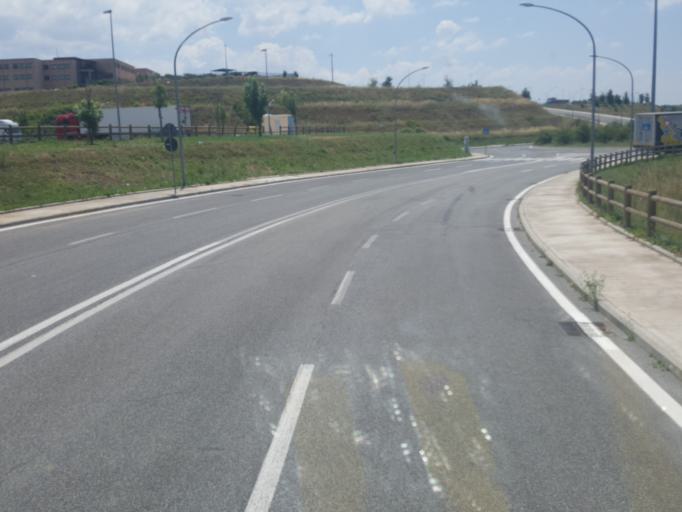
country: IT
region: Latium
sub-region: Citta metropolitana di Roma Capitale
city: Fiano Romano
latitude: 42.1670
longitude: 12.6500
